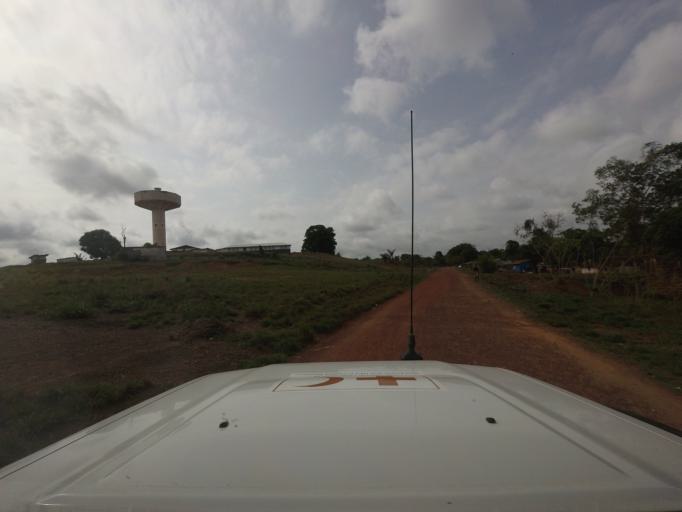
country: LR
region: Bong
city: Gbarnga
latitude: 7.0067
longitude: -9.4746
